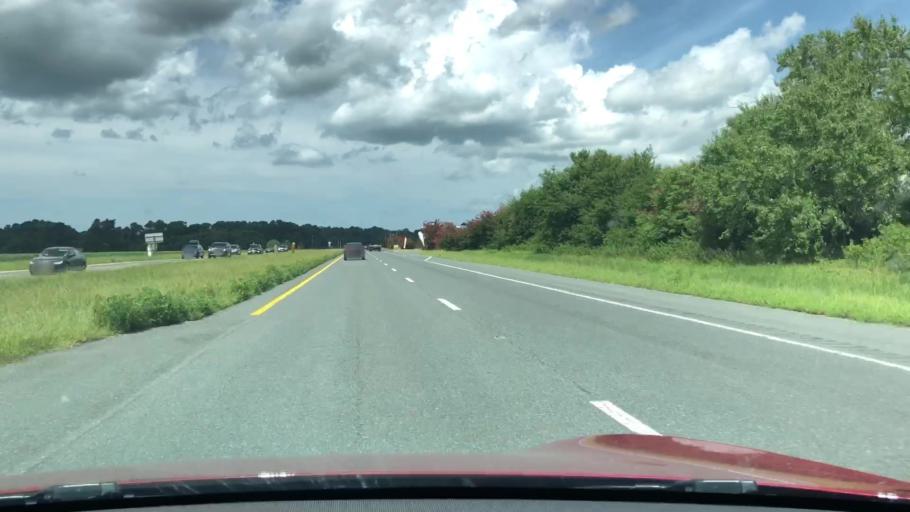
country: US
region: Virginia
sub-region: Northampton County
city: Cape Charles
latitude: 37.2755
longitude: -75.9765
